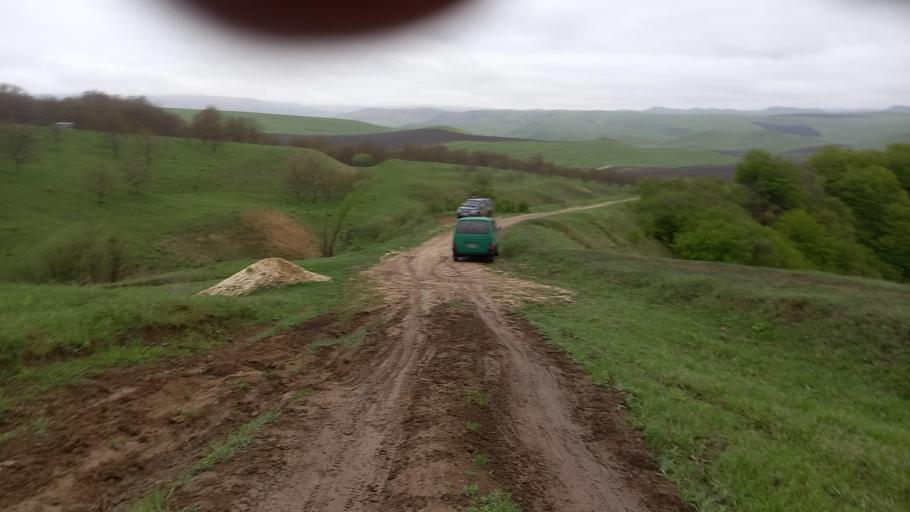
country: RU
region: Kabardino-Balkariya
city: Kamennomostskoye
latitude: 43.7076
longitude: 43.0762
